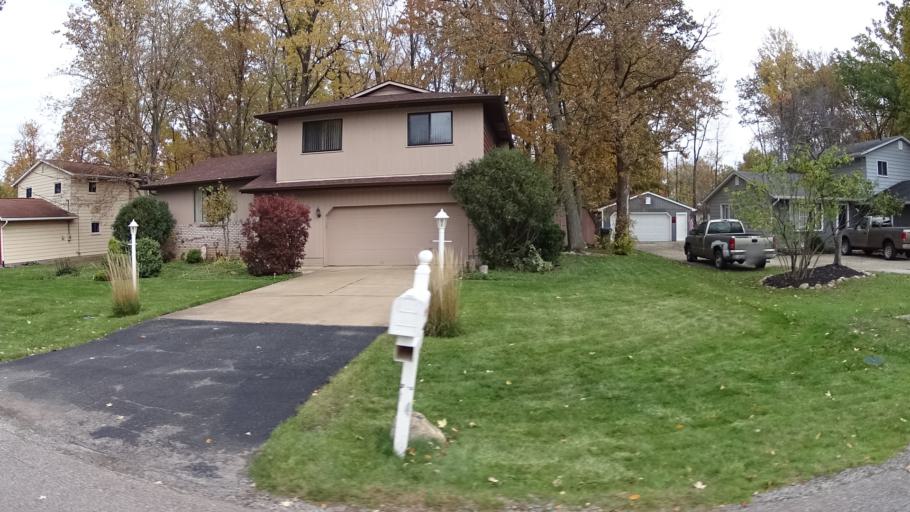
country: US
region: Ohio
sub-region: Lorain County
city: Sheffield Lake
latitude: 41.4842
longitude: -82.0994
